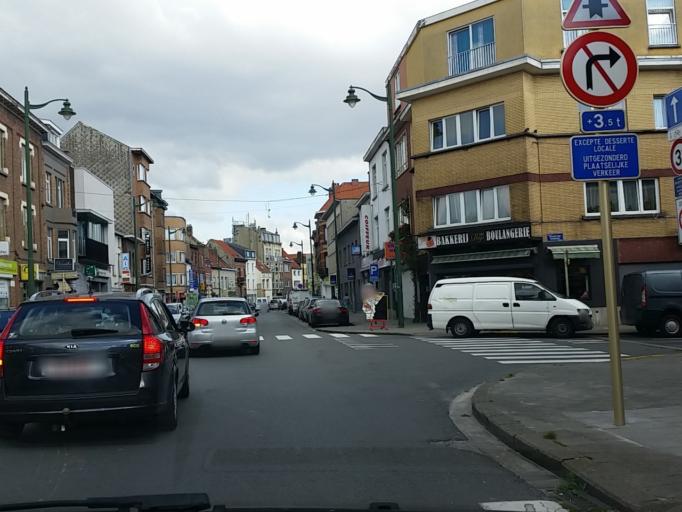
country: BE
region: Flanders
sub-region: Provincie Vlaams-Brabant
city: Drogenbos
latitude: 50.8233
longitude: 4.2953
